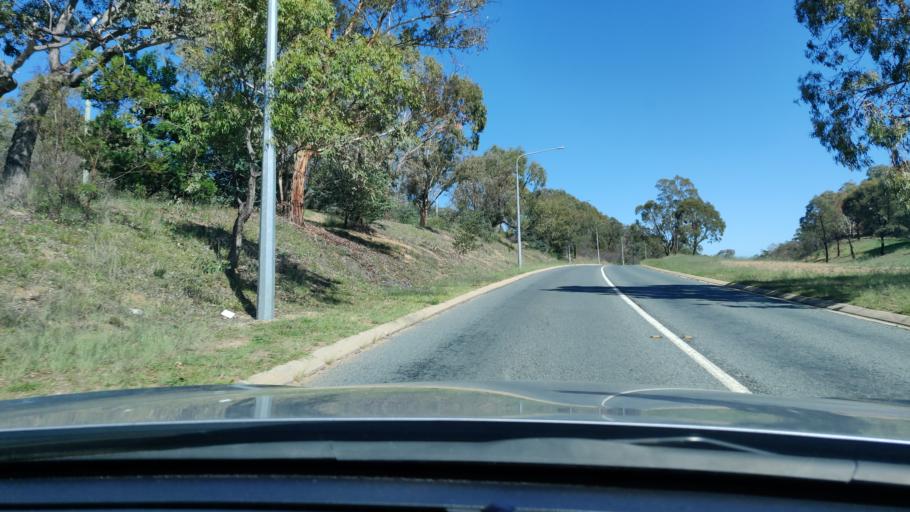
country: AU
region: Australian Capital Territory
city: Macarthur
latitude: -35.4455
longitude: 149.1130
